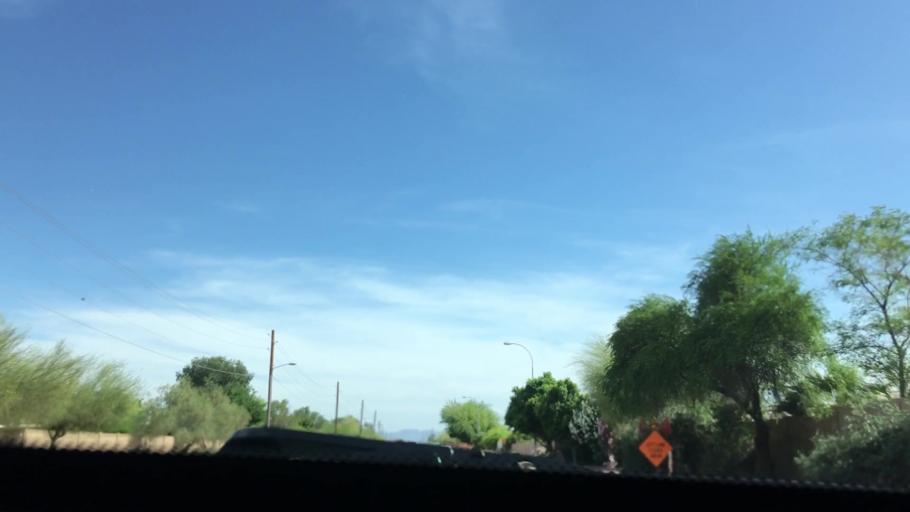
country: US
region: Arizona
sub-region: Maricopa County
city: Peoria
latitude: 33.6015
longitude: -112.2202
